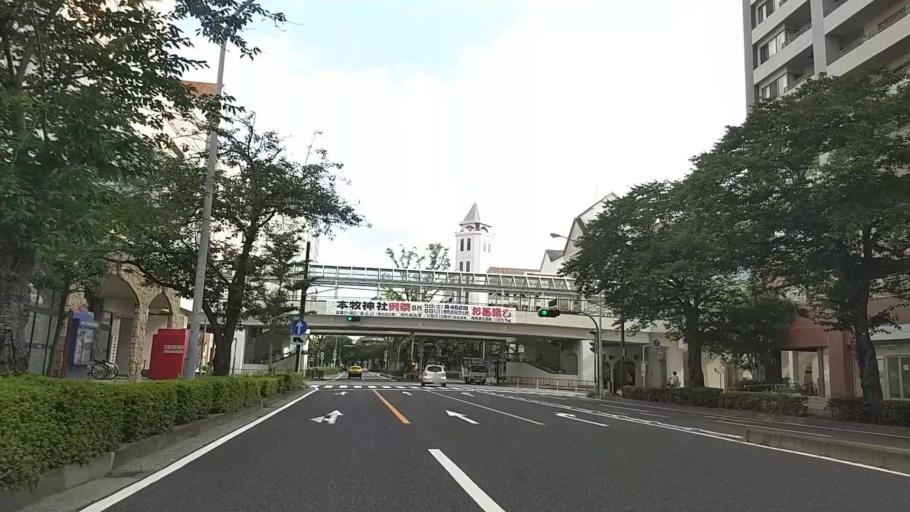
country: JP
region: Kanagawa
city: Yokohama
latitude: 35.4245
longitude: 139.6659
